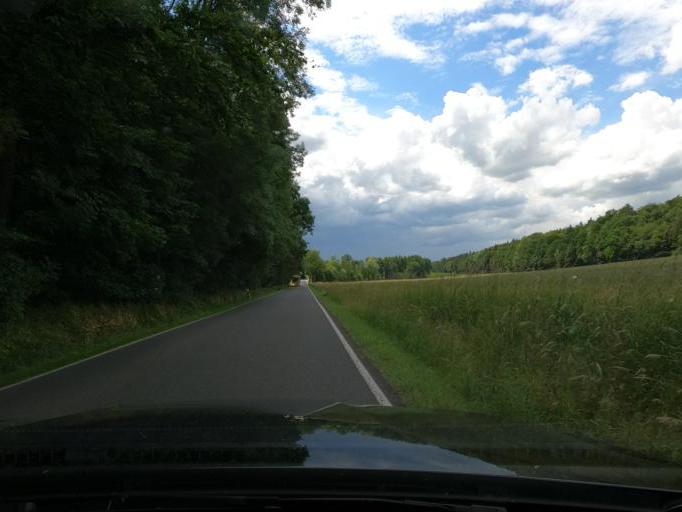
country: DE
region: Lower Saxony
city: Elbe
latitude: 52.1110
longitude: 10.2728
